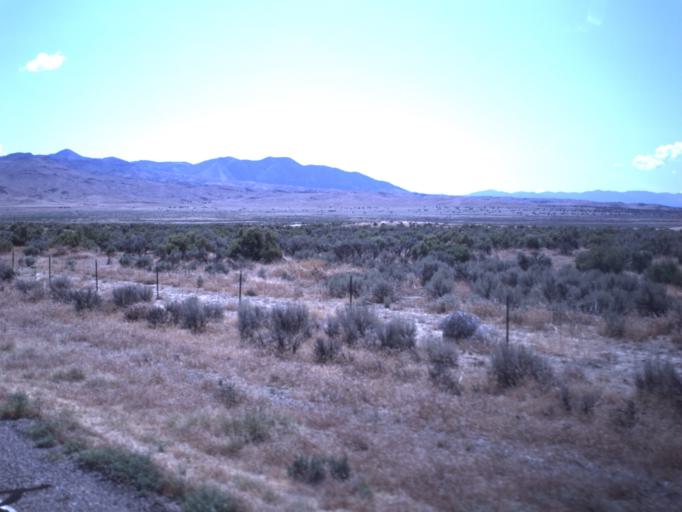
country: US
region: Utah
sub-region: Millard County
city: Delta
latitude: 39.3540
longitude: -112.4324
